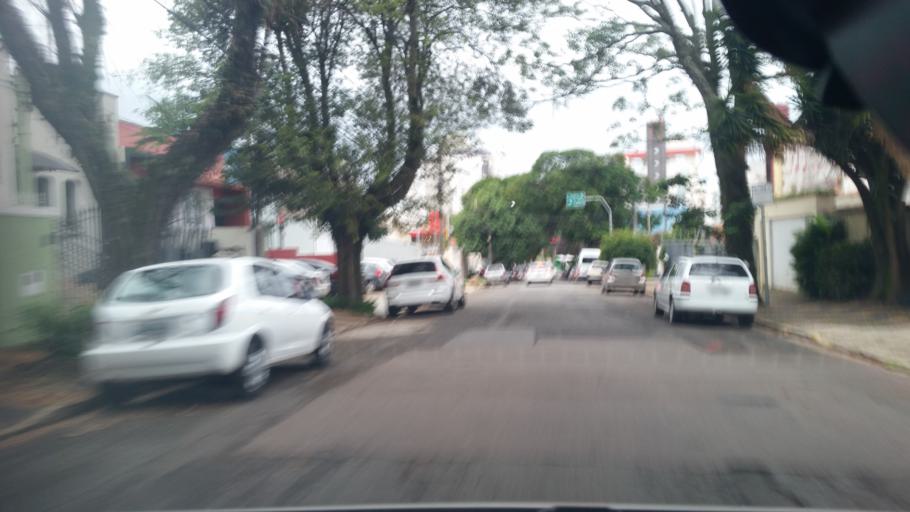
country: BR
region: Sao Paulo
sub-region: Campinas
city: Campinas
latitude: -22.8859
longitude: -47.0703
